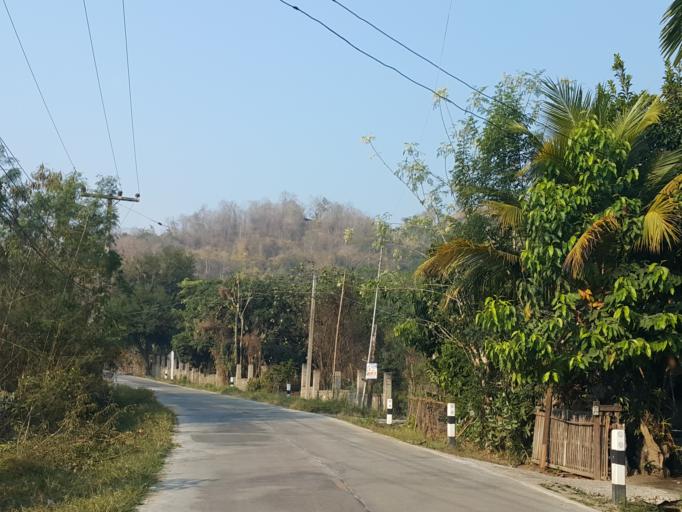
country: TH
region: Chiang Mai
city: Hang Dong
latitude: 18.7594
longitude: 98.8703
